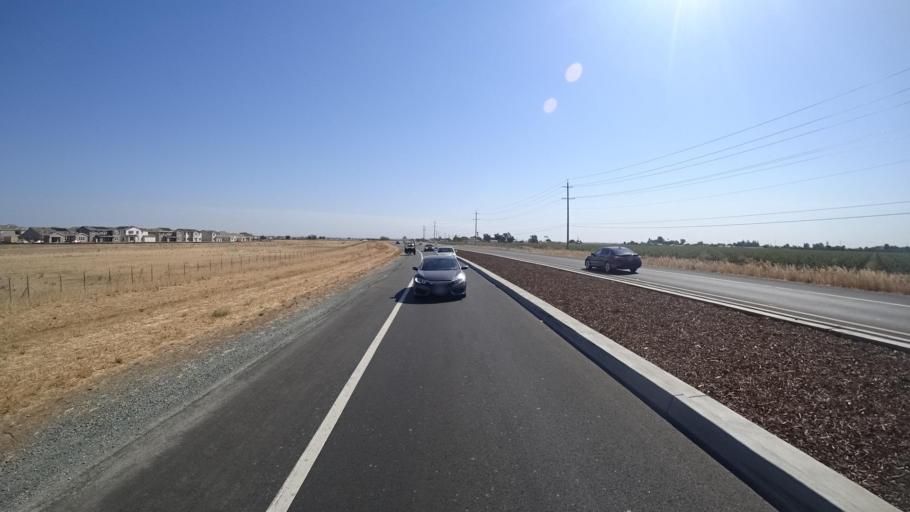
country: US
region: California
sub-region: Sacramento County
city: Laguna
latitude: 38.3714
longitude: -121.4147
